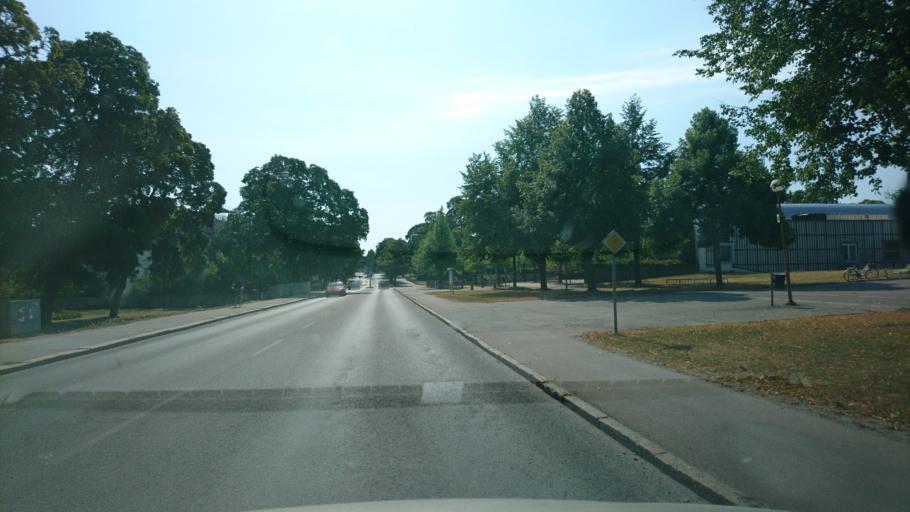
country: SE
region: Uppsala
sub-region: Uppsala Kommun
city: Uppsala
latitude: 59.8600
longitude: 17.6209
